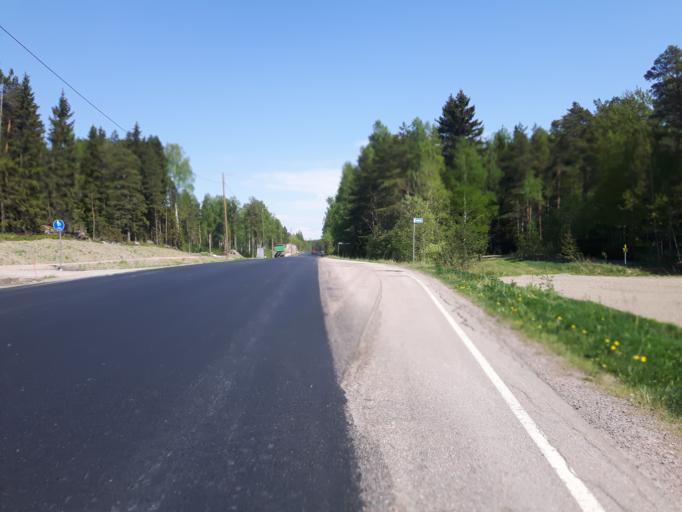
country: FI
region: Uusimaa
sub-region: Porvoo
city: Porvoo
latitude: 60.3608
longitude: 25.5385
